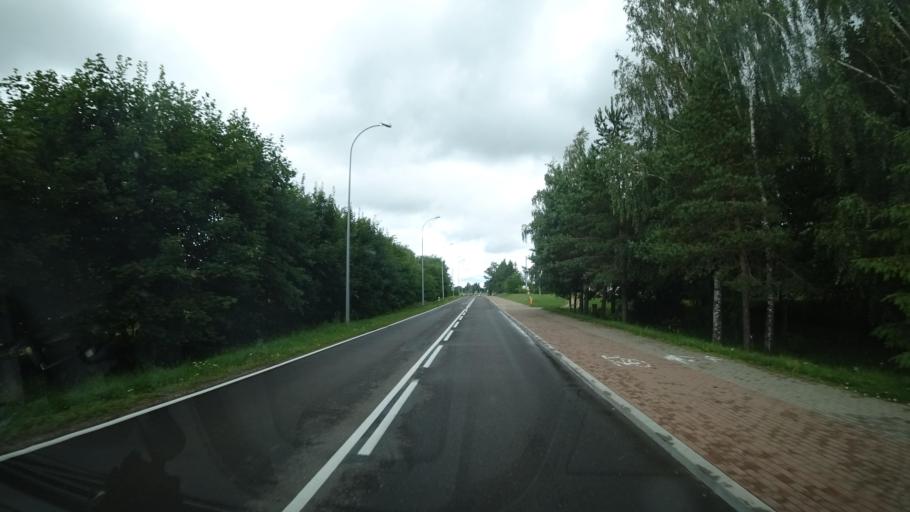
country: PL
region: Warmian-Masurian Voivodeship
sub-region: Powiat olecki
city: Kowale Oleckie
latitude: 54.1705
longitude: 22.4142
